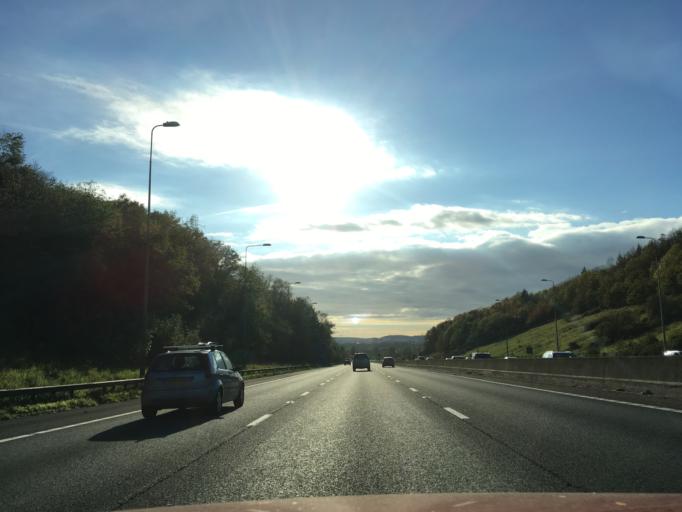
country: GB
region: England
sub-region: South Gloucestershire
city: Severn Beach
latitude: 51.5186
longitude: -2.6382
